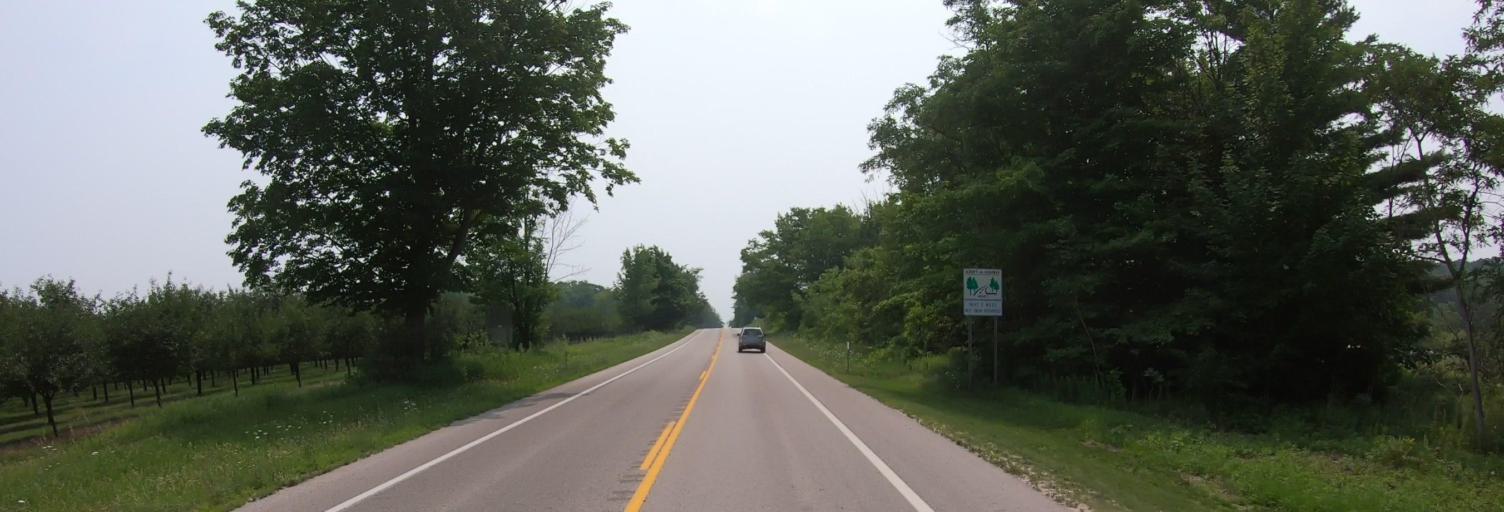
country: US
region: Michigan
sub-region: Leelanau County
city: Leland
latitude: 45.0654
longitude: -85.5873
